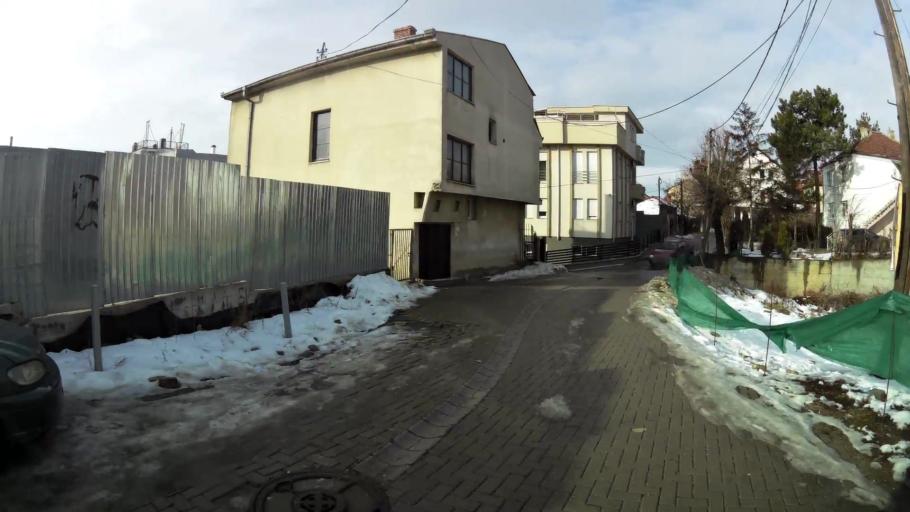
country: XK
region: Pristina
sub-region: Komuna e Prishtines
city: Pristina
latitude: 42.6673
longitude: 21.1747
